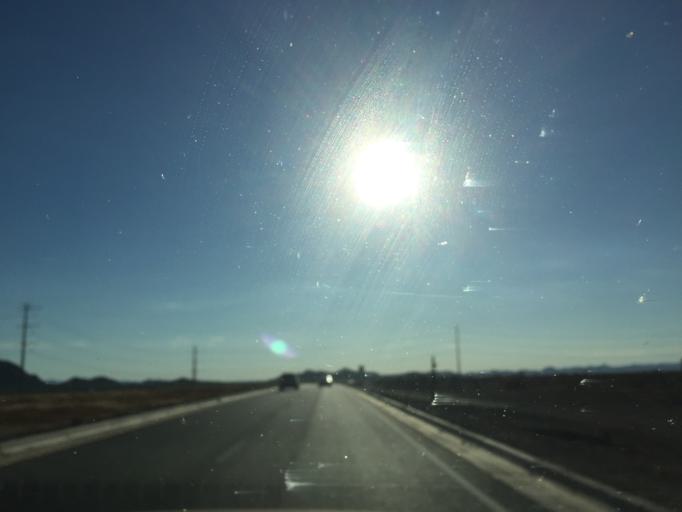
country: US
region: Arizona
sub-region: Maricopa County
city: Anthem
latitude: 33.7699
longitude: -112.1364
